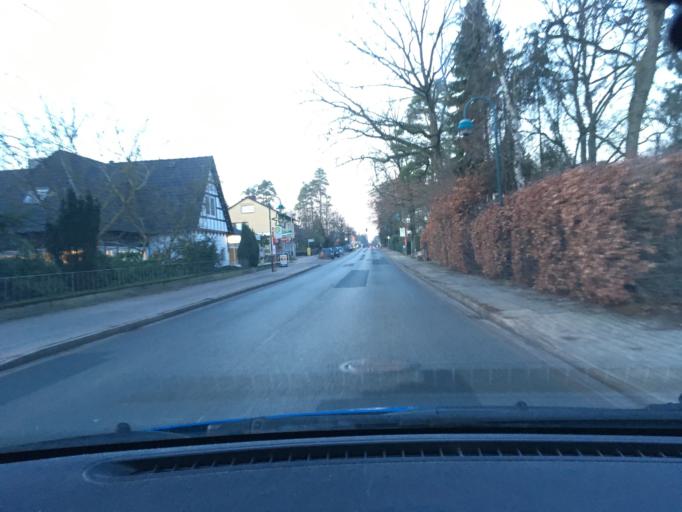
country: DE
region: Lower Saxony
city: Buchholz in der Nordheide
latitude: 53.2823
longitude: 9.8718
